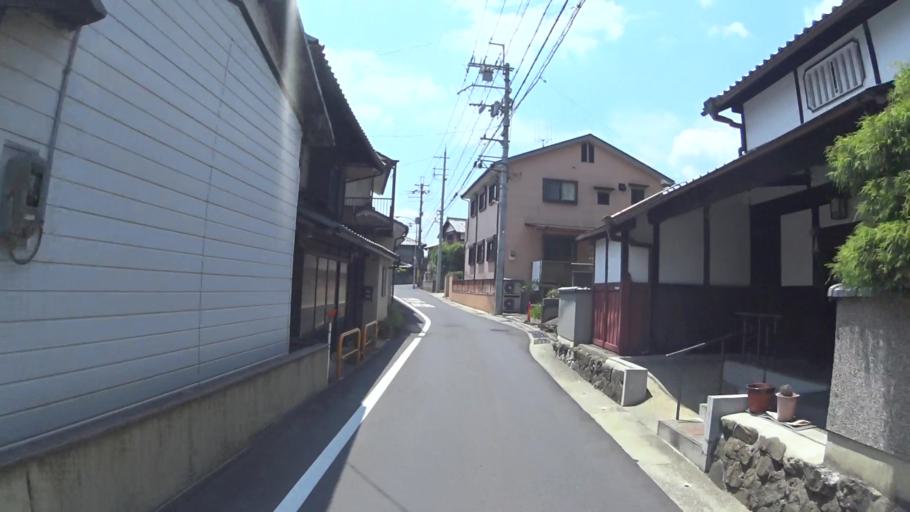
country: JP
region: Kyoto
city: Muko
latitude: 34.9580
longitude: 135.6604
